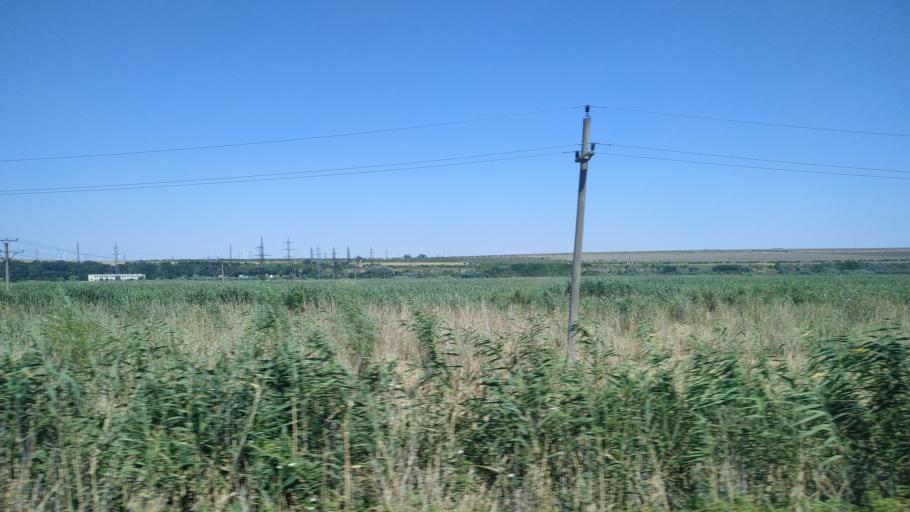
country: RO
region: Constanta
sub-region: Comuna Mircea Voda
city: Satu Nou
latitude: 44.2618
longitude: 28.1988
